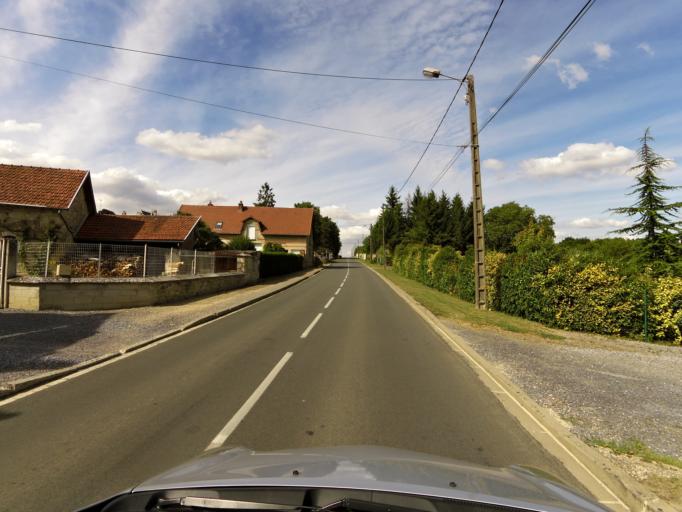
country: FR
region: Picardie
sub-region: Departement de l'Aisne
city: Bruyeres-et-Montberault
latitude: 49.4872
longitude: 3.6676
